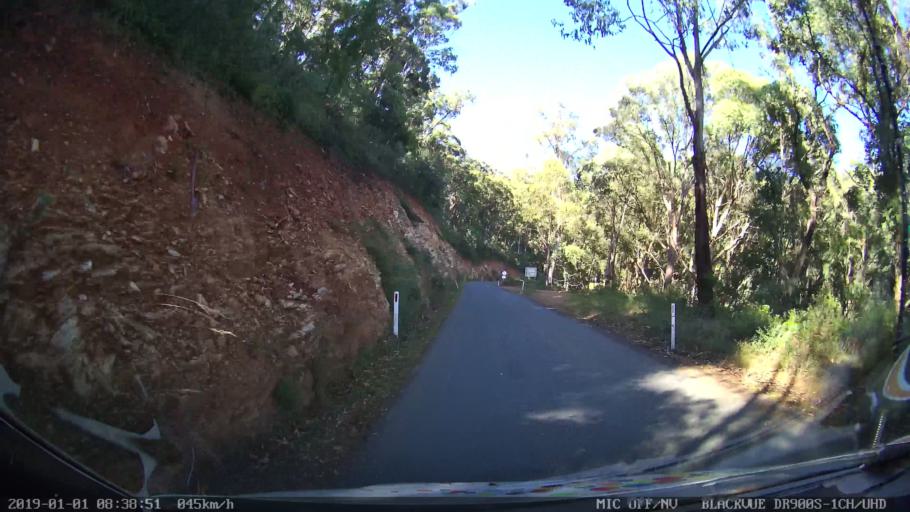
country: AU
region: New South Wales
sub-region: Snowy River
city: Jindabyne
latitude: -36.3327
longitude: 148.1955
